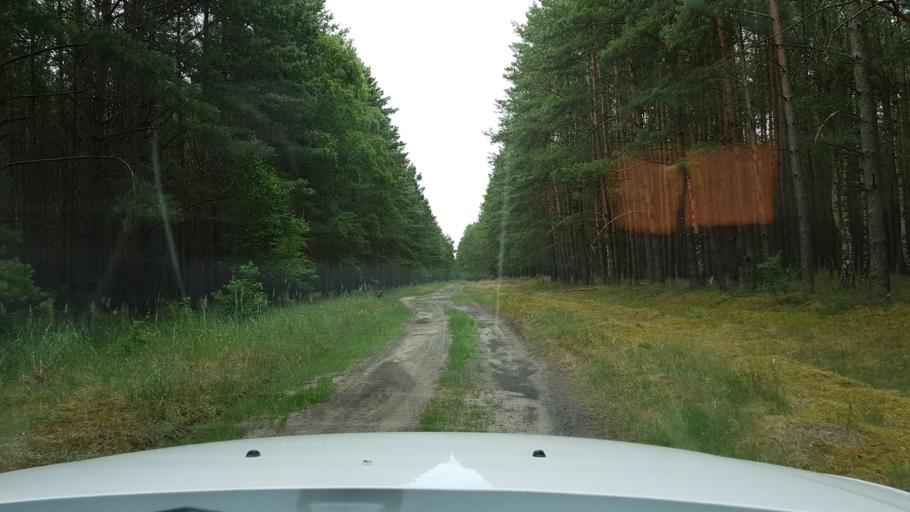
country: PL
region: West Pomeranian Voivodeship
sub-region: Powiat mysliborski
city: Boleszkowice
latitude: 52.6520
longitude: 14.5616
